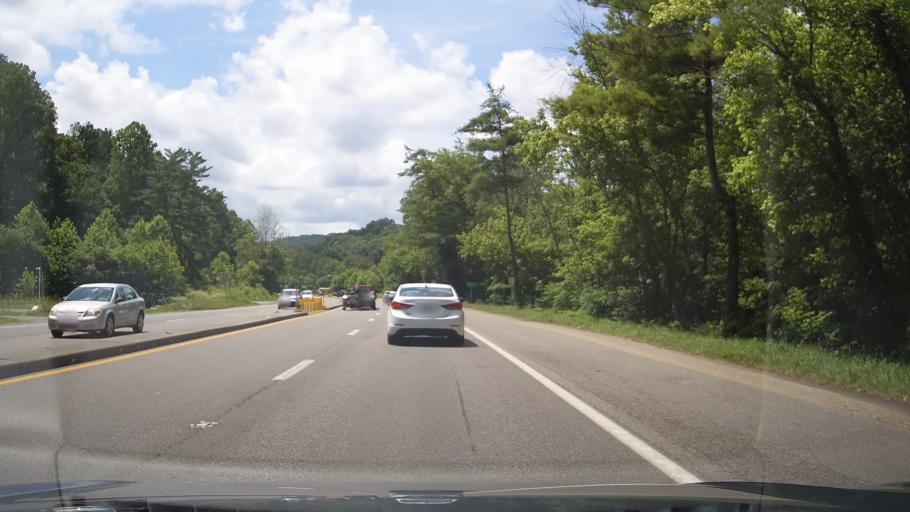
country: US
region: Virginia
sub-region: Scott County
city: Weber City
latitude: 36.6361
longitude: -82.5532
